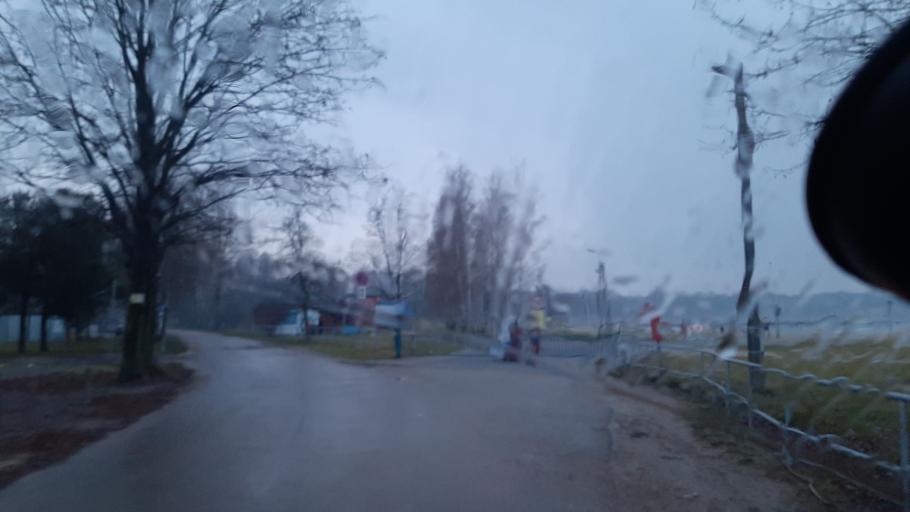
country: PL
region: Lublin Voivodeship
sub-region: Powiat lubartowski
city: Firlej
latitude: 51.5577
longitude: 22.5234
